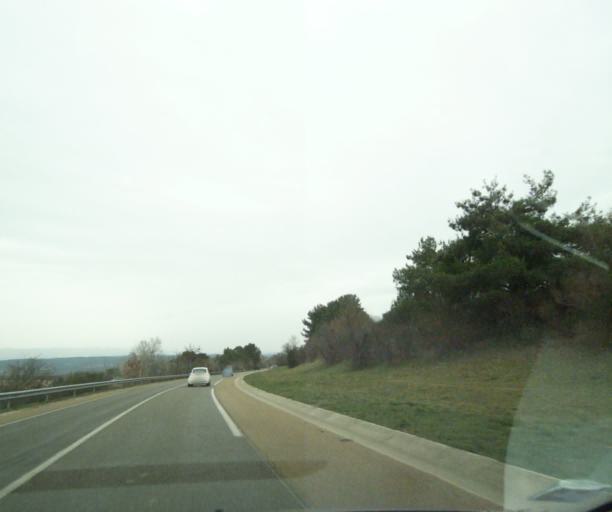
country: FR
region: Provence-Alpes-Cote d'Azur
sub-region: Departement des Bouches-du-Rhone
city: Le Puy-Sainte-Reparade
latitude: 43.6590
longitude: 5.4253
